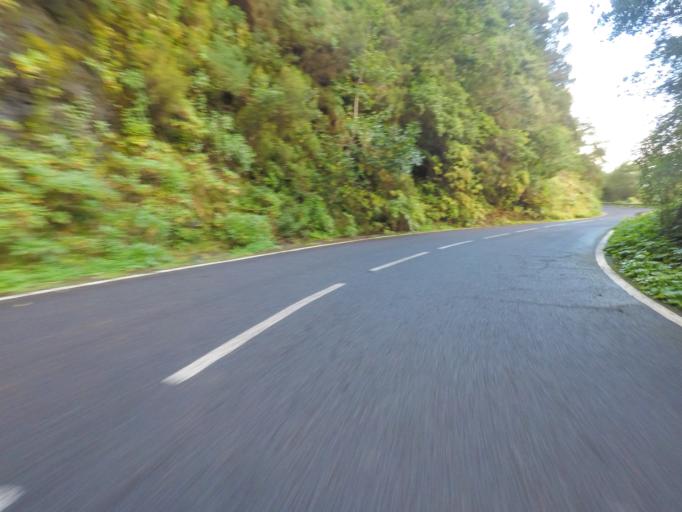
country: ES
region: Canary Islands
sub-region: Provincia de Santa Cruz de Tenerife
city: Hermigua
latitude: 28.1248
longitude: -17.2055
